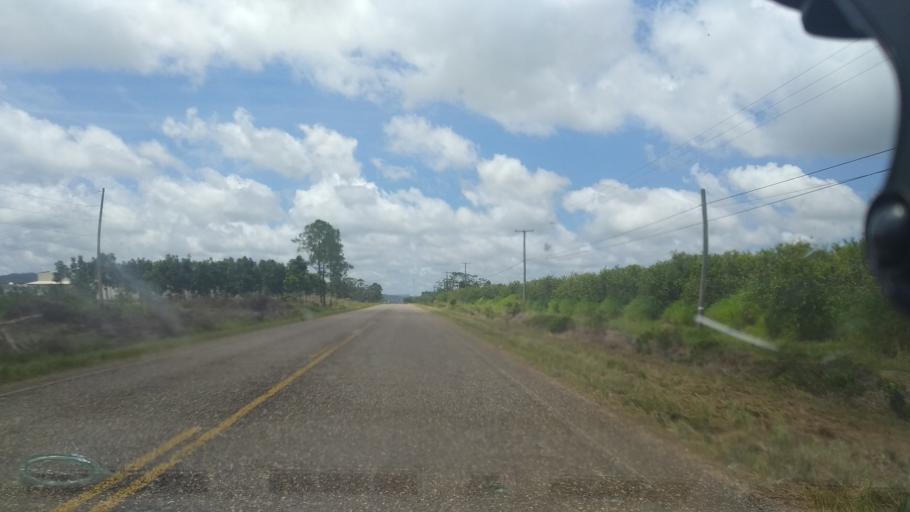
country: BZ
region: Stann Creek
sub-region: Dangriga
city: Dangriga
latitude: 16.7891
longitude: -88.3807
